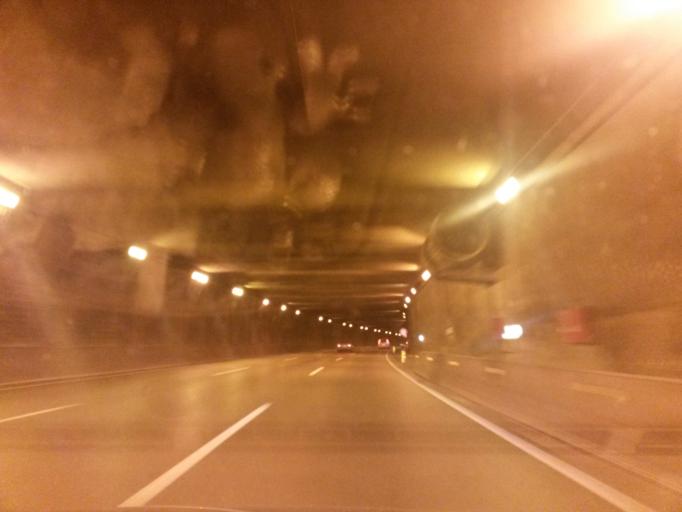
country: ES
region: Catalonia
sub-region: Provincia de Barcelona
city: Montgat
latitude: 41.4712
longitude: 2.2778
